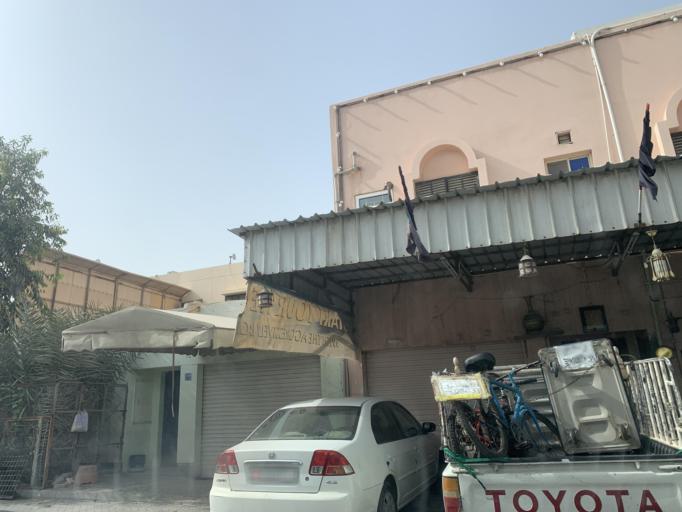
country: BH
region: Northern
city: Madinat `Isa
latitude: 26.1775
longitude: 50.5236
